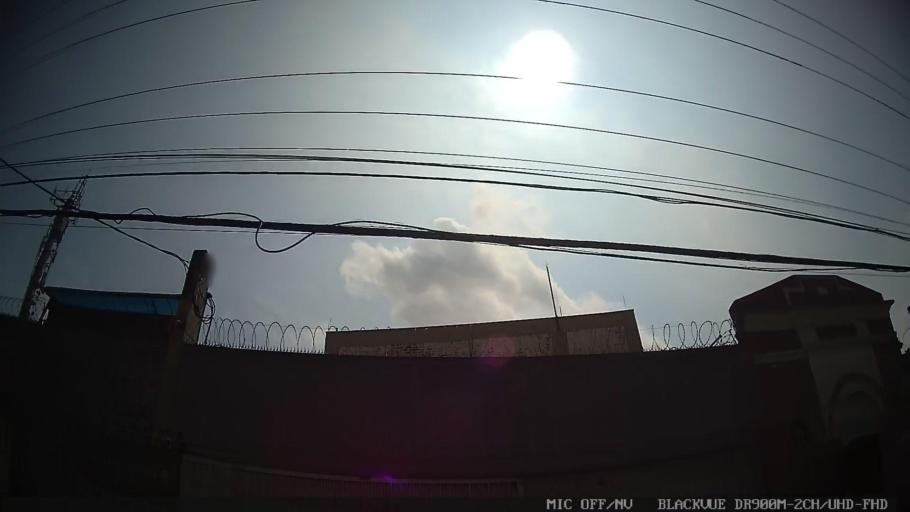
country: BR
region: Sao Paulo
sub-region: Taboao Da Serra
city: Taboao da Serra
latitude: -23.6485
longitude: -46.7100
